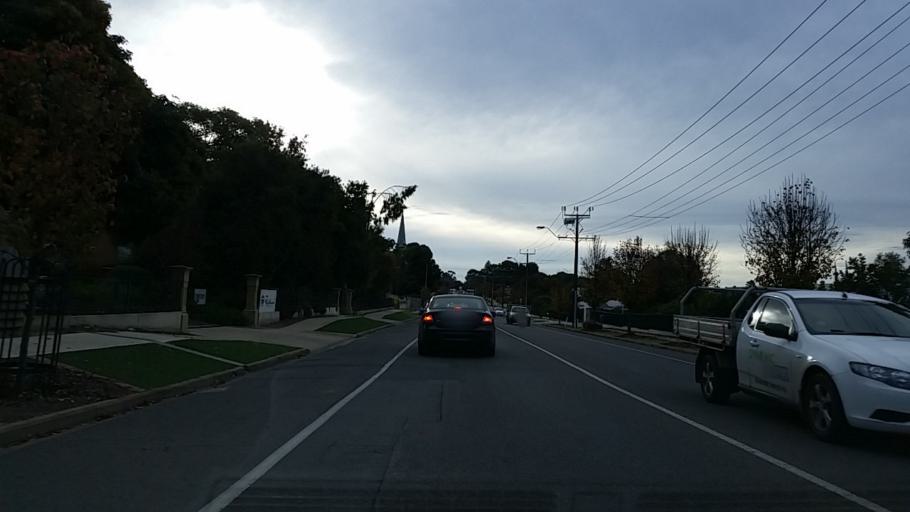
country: AU
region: South Australia
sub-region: Murray Bridge
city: Murray Bridge
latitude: -35.1254
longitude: 139.2773
